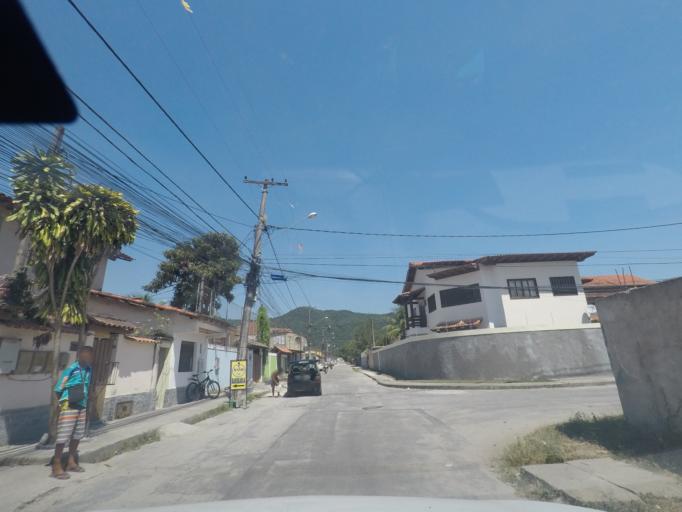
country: BR
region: Rio de Janeiro
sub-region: Niteroi
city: Niteroi
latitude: -22.9389
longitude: -43.0220
